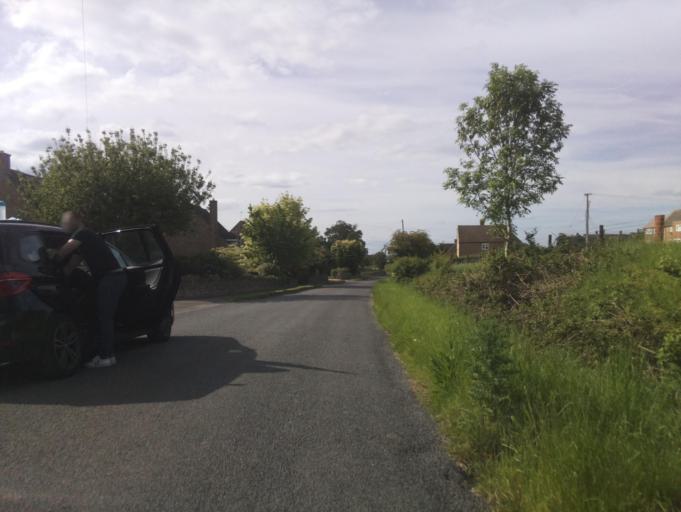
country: GB
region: England
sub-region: Gloucestershire
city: Chipping Campden
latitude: 52.0662
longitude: -1.8154
